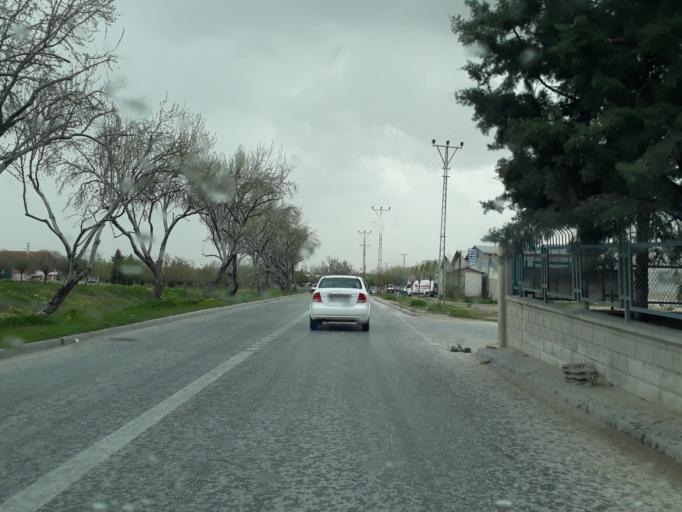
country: TR
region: Konya
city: Selcuklu
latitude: 37.9179
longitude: 32.4736
